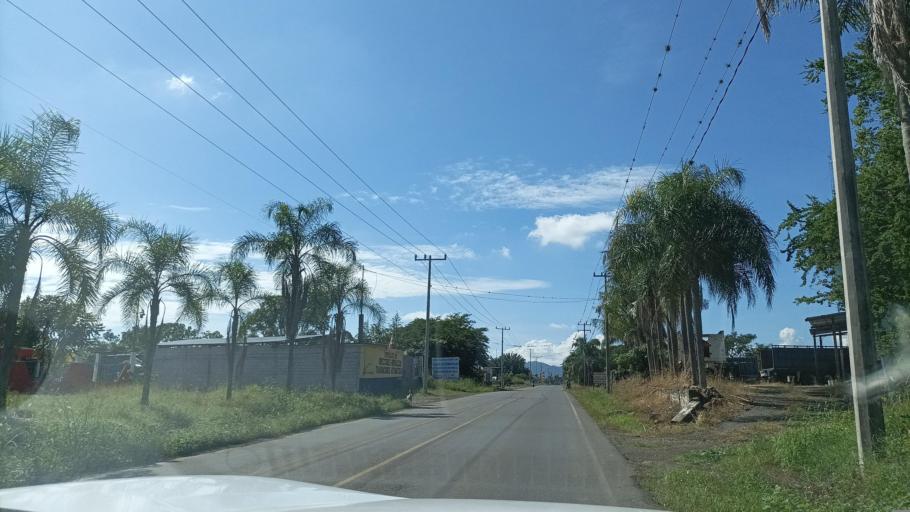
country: MX
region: Veracruz
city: Paso del Macho
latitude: 18.9692
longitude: -96.7326
